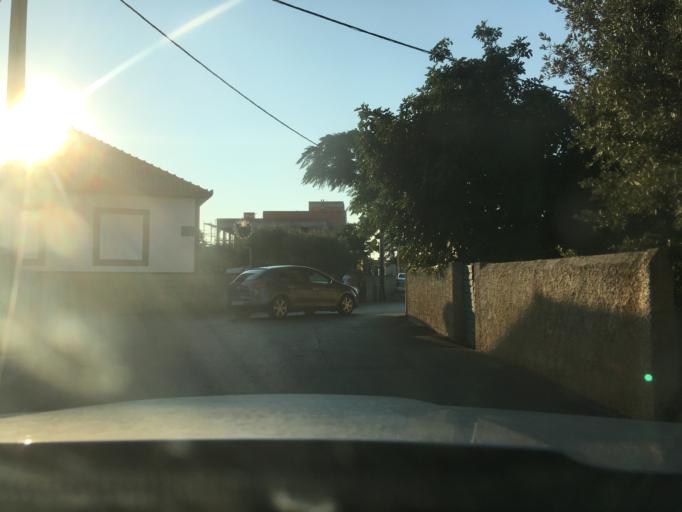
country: HR
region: Zadarska
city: Vir
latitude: 44.3050
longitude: 15.0785
